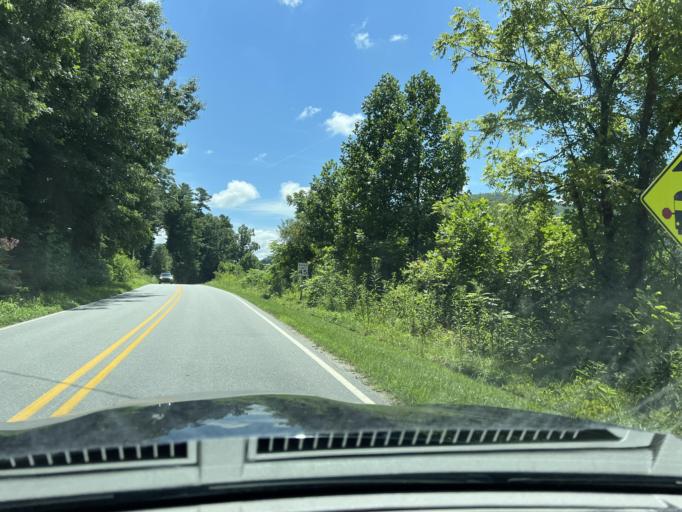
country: US
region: North Carolina
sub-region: Henderson County
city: Hoopers Creek
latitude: 35.4397
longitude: -82.4390
